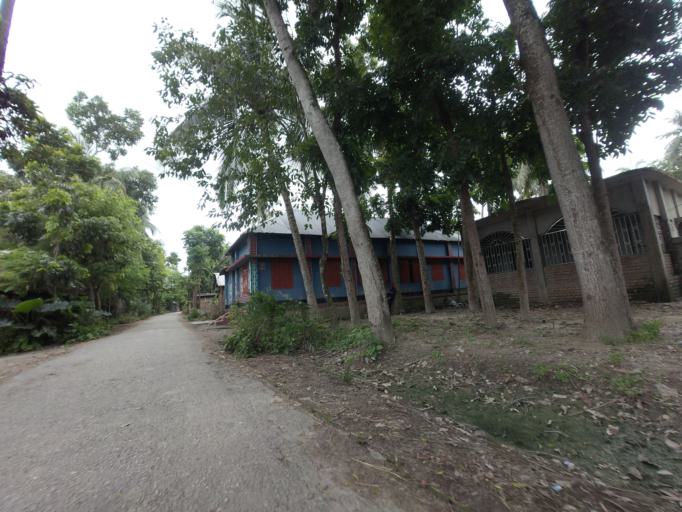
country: BD
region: Khulna
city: Kalia
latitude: 23.0476
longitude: 89.6462
